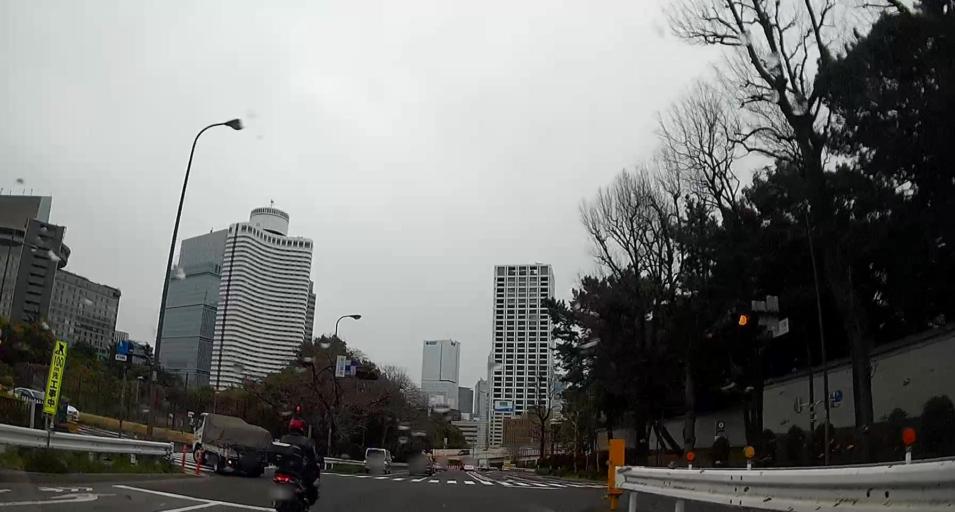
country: JP
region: Tokyo
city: Tokyo
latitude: 35.6809
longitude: 139.7314
